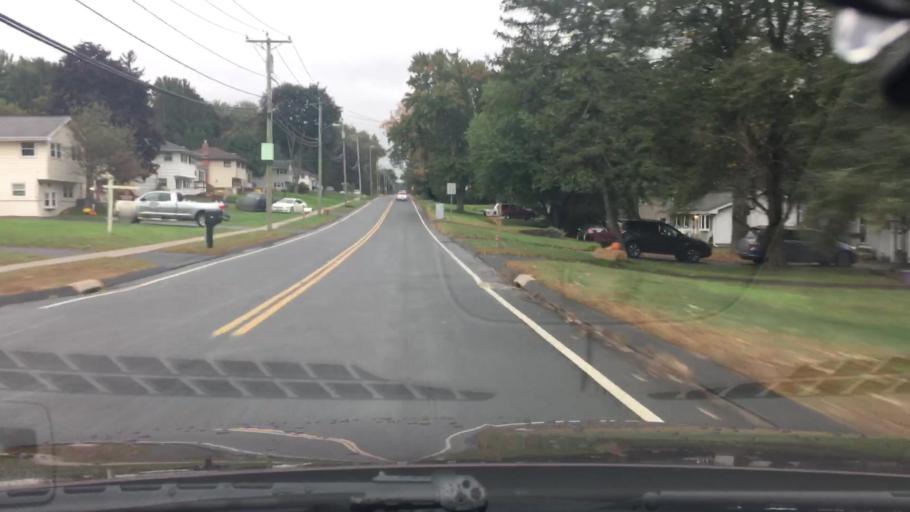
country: US
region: Connecticut
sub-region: Hartford County
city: Manchester
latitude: 41.8274
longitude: -72.5161
